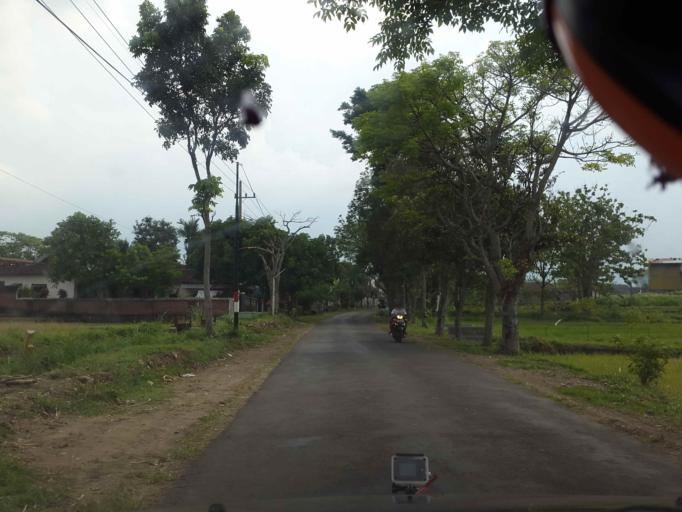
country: ID
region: East Java
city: Madiun
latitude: -7.6675
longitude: 111.3139
